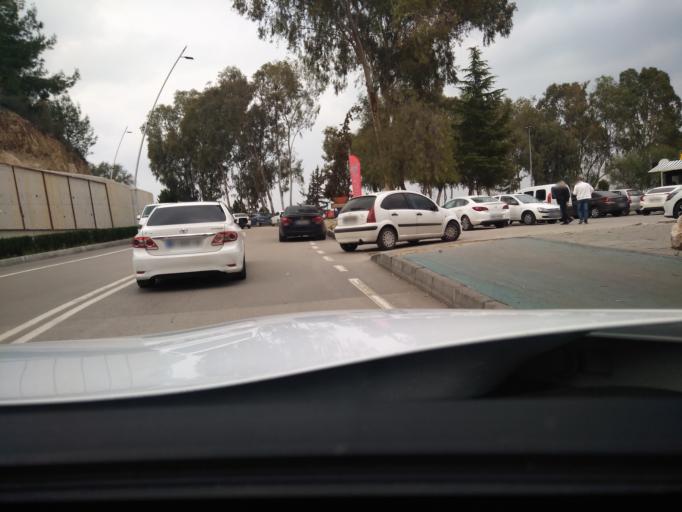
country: TR
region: Adana
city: Adana
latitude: 37.0572
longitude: 35.3050
